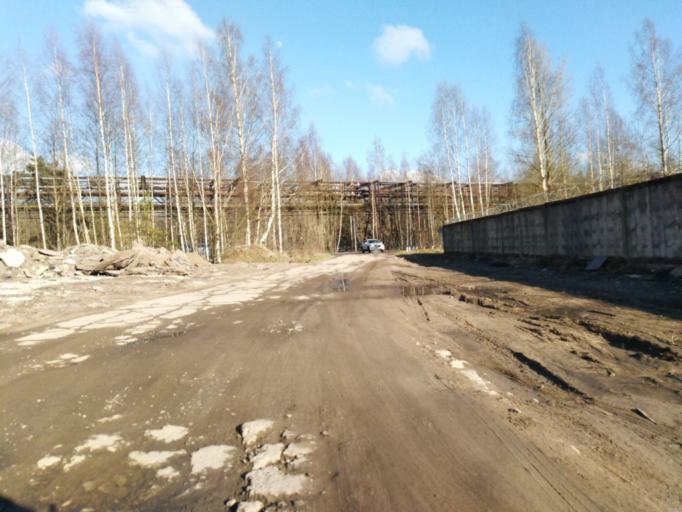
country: RU
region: Leningrad
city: Novoye Devyatkino
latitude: 60.0717
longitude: 30.4807
